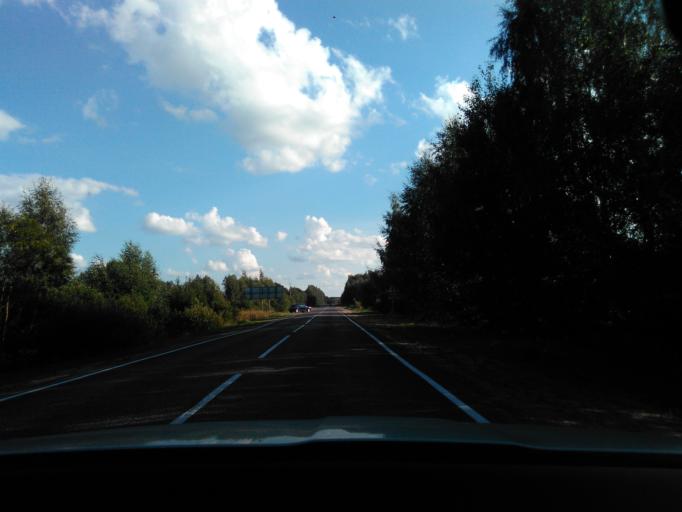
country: RU
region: Tverskaya
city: Zavidovo
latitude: 56.6085
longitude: 36.5429
